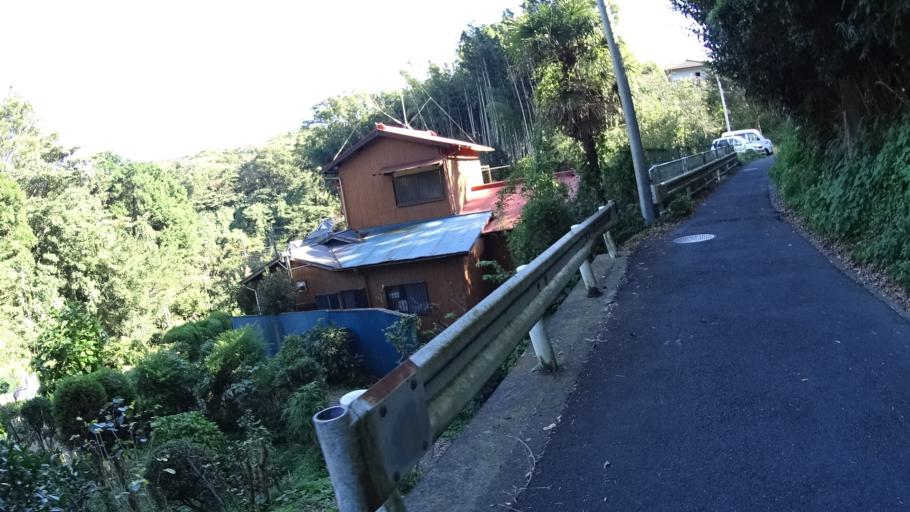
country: JP
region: Kanagawa
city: Kamakura
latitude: 35.3677
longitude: 139.5997
